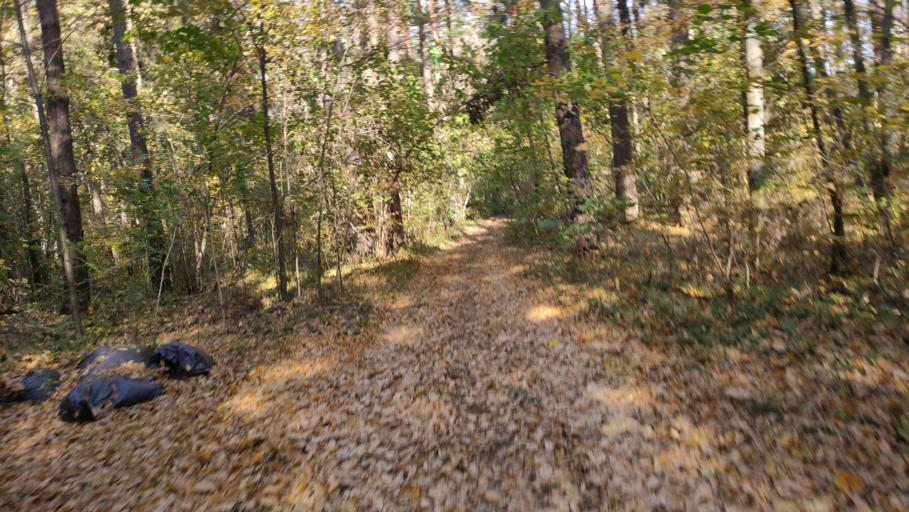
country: LT
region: Alytaus apskritis
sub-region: Alytus
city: Alytus
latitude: 54.3704
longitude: 24.0911
